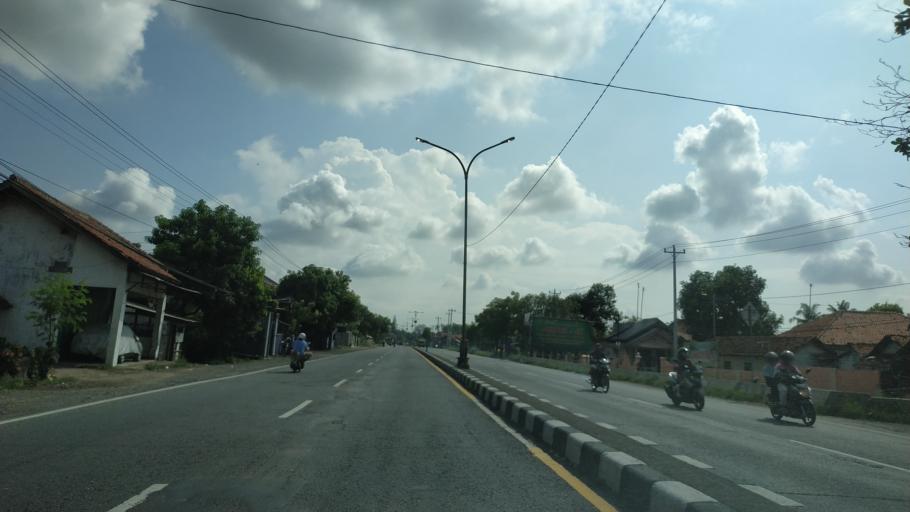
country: ID
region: Central Java
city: Comal
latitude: -6.8942
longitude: 109.5422
